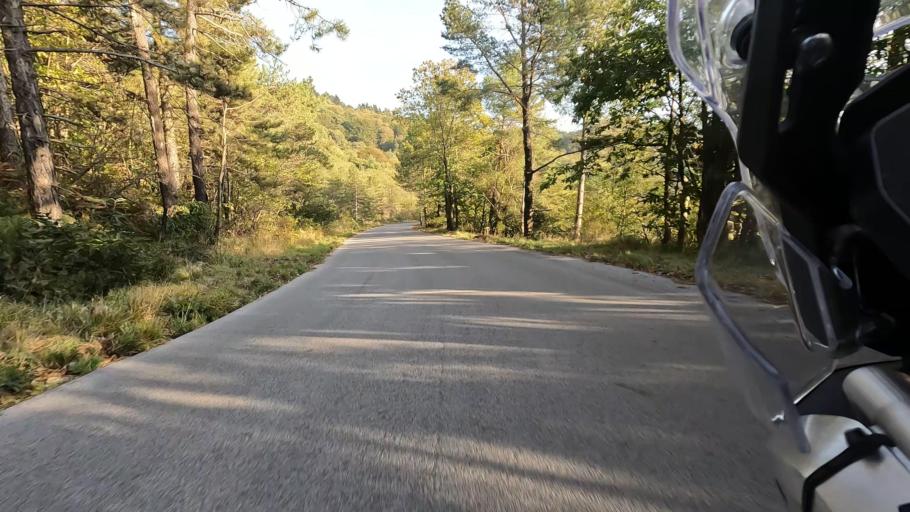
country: IT
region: Liguria
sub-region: Provincia di Savona
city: San Giovanni
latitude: 44.4204
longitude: 8.5280
